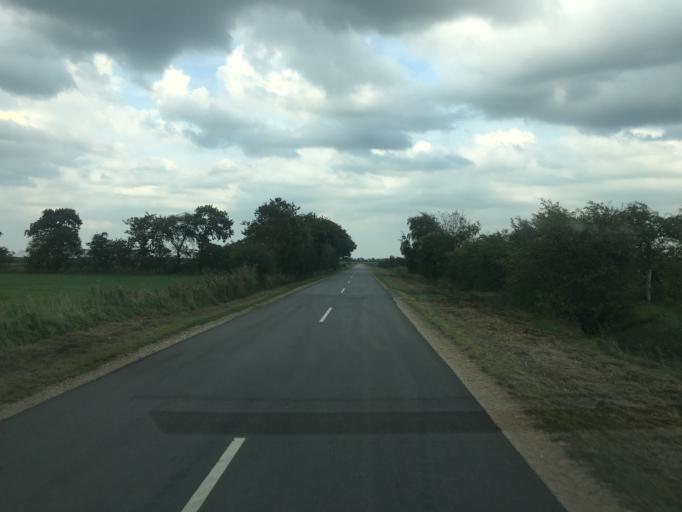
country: DK
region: South Denmark
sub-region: Tonder Kommune
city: Logumkloster
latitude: 55.0611
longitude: 9.0542
